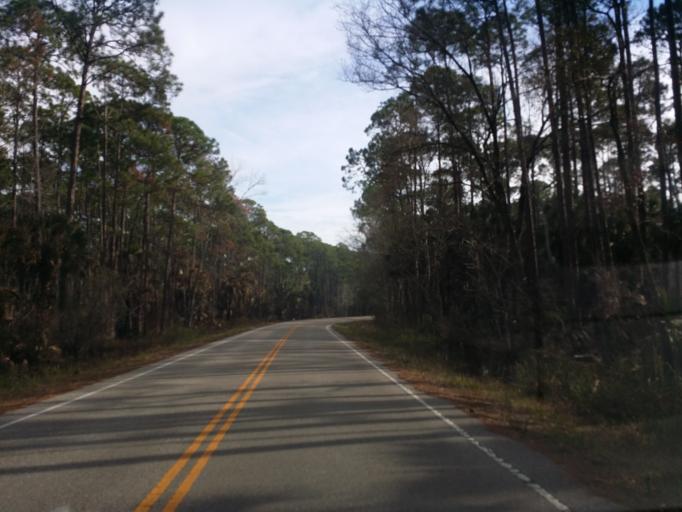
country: US
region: Florida
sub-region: Leon County
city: Woodville
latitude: 30.1508
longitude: -84.1442
